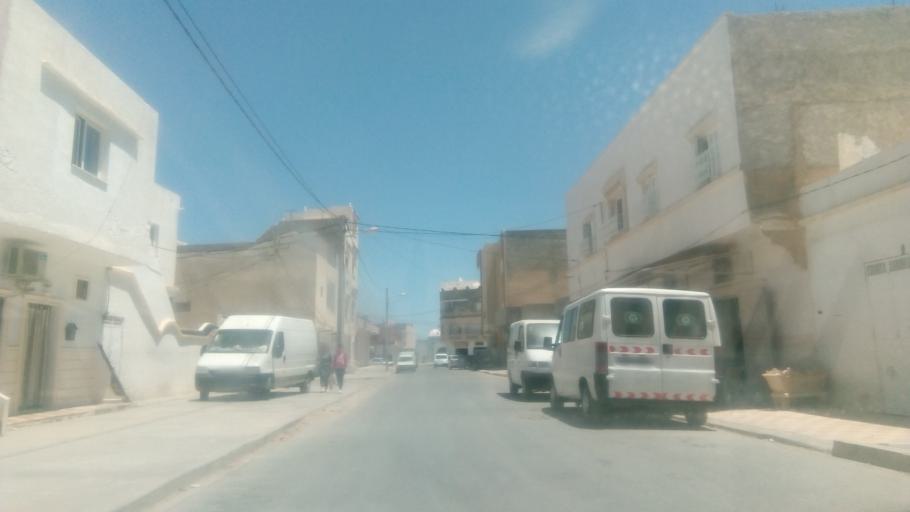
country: TN
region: Al Qayrawan
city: Kairouan
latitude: 35.6687
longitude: 10.0879
